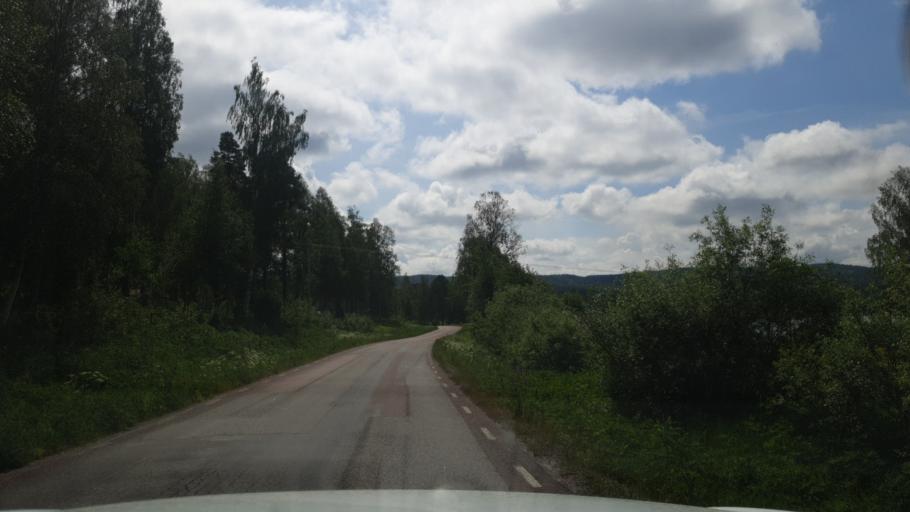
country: SE
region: Vaermland
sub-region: Arvika Kommun
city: Arvika
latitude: 59.5287
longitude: 12.8254
